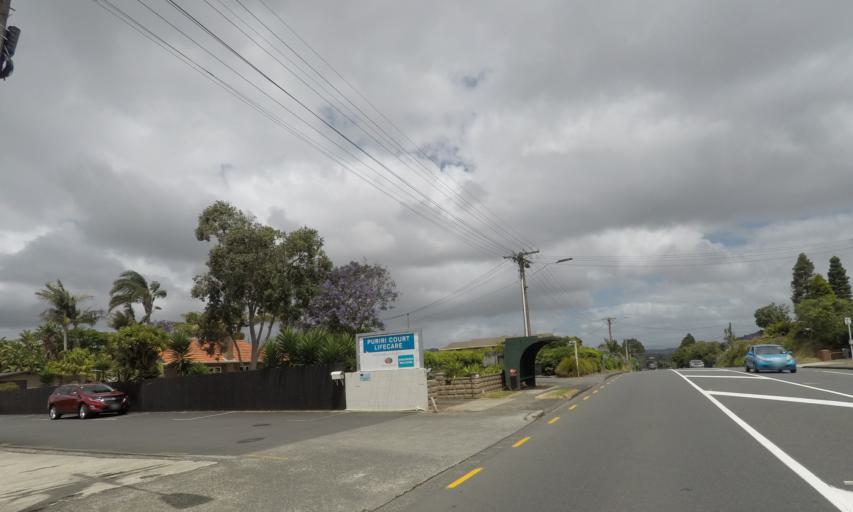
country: NZ
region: Northland
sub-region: Whangarei
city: Whangarei
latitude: -35.6952
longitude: 174.3116
